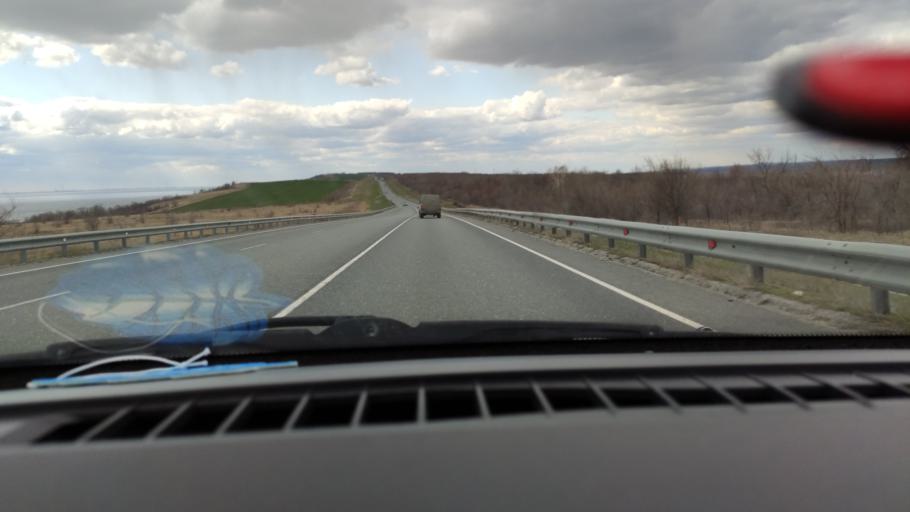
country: RU
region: Saratov
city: Balakovo
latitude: 52.1972
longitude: 47.8602
